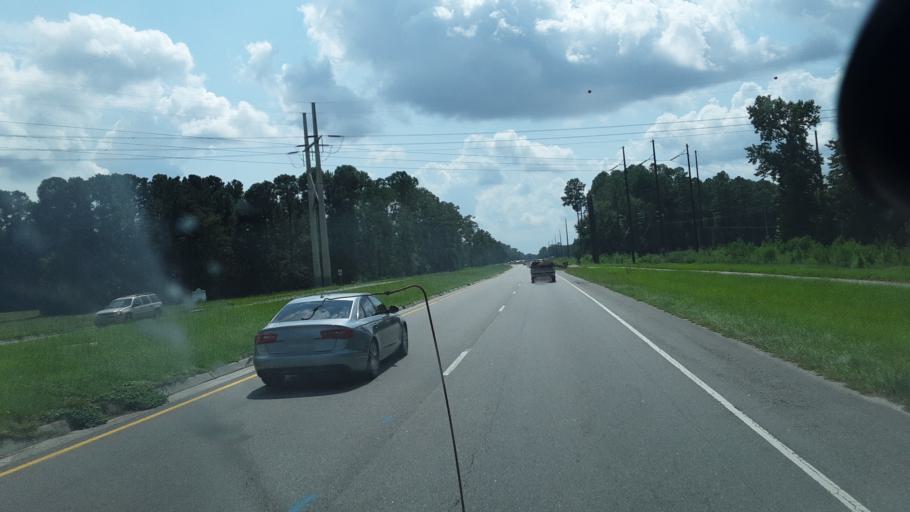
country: US
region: South Carolina
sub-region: Beaufort County
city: Bluffton
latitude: 32.2676
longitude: -80.9559
